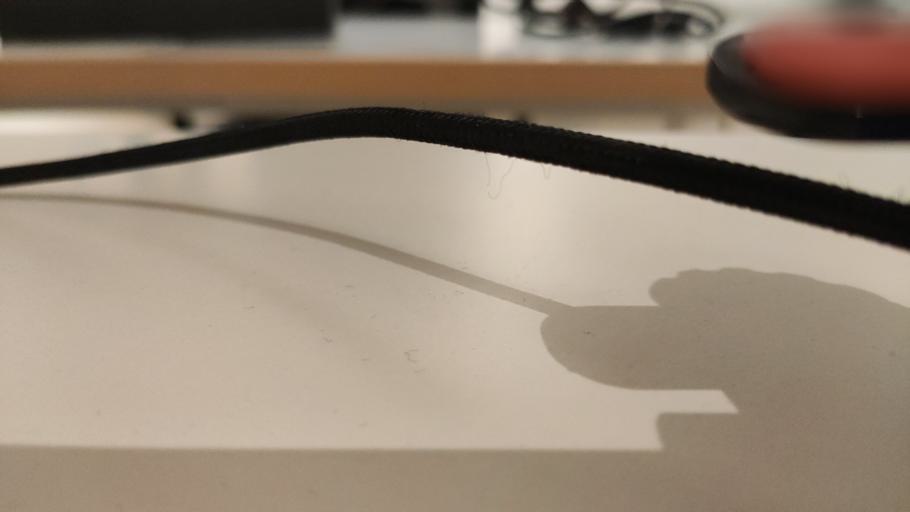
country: RU
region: Moskovskaya
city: Dorokhovo
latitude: 55.5307
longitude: 36.3590
